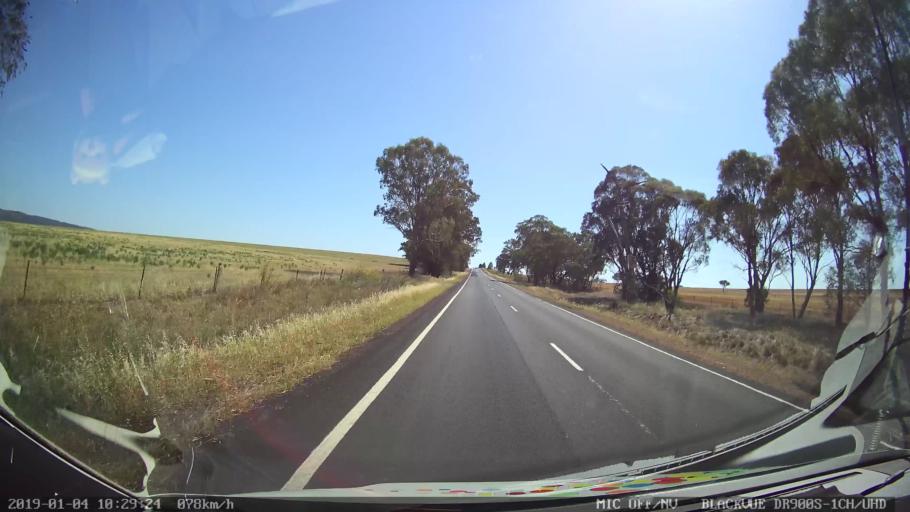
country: AU
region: New South Wales
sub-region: Cabonne
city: Canowindra
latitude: -33.3559
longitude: 148.6198
